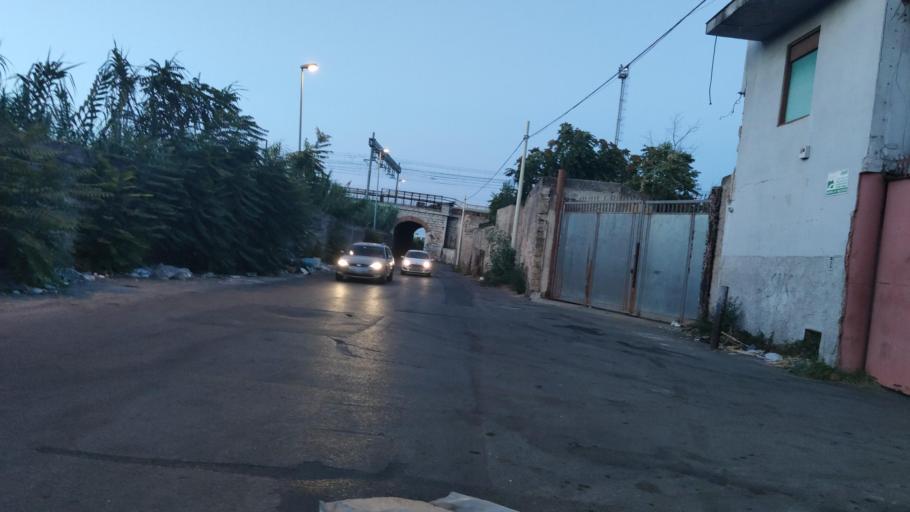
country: IT
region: Sicily
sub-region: Palermo
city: Ciaculli
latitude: 38.1041
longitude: 13.3729
